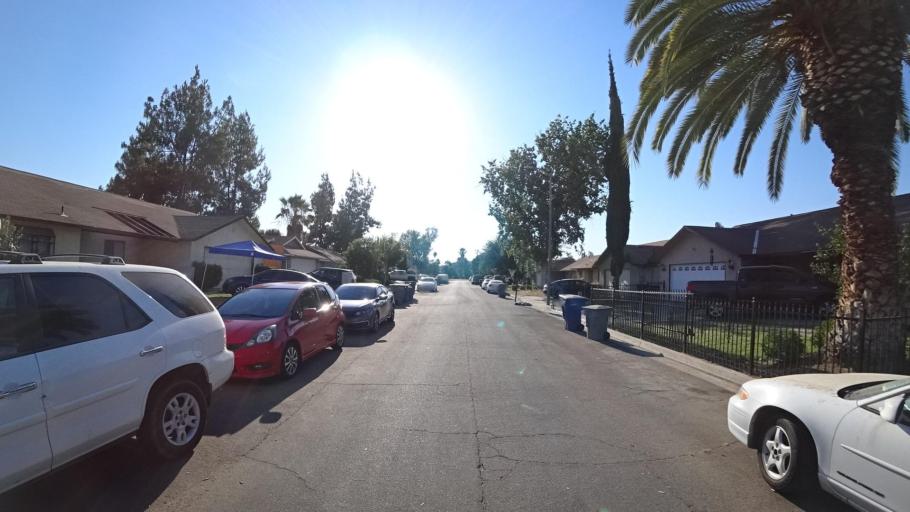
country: US
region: California
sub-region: Fresno County
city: Sunnyside
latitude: 36.7413
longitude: -119.7289
